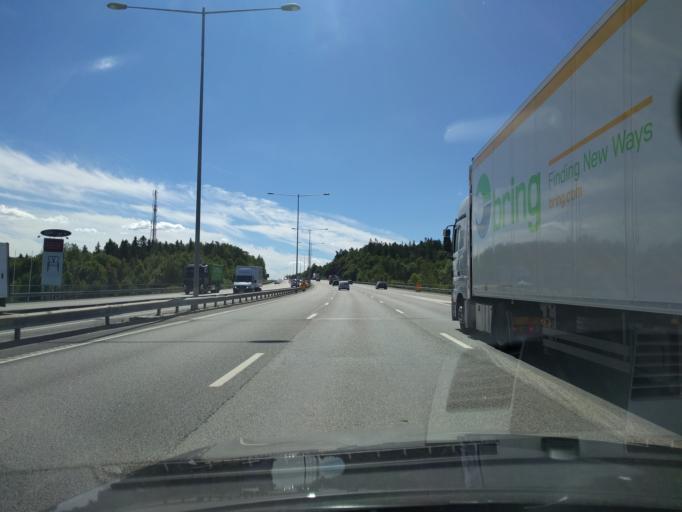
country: SE
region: Stockholm
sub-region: Haninge Kommun
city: Handen
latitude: 59.1982
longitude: 18.1334
